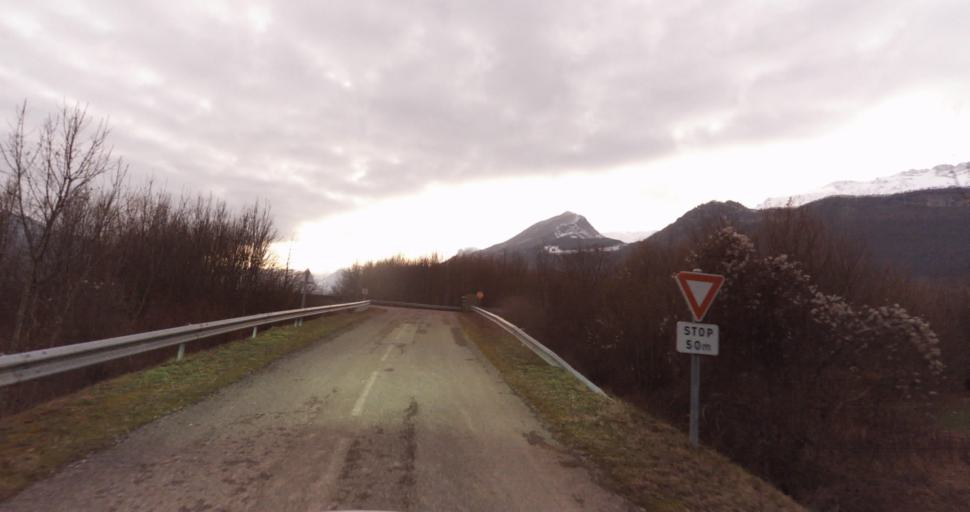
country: FR
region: Rhone-Alpes
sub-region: Departement de l'Isere
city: Vif
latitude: 45.0685
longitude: 5.6823
